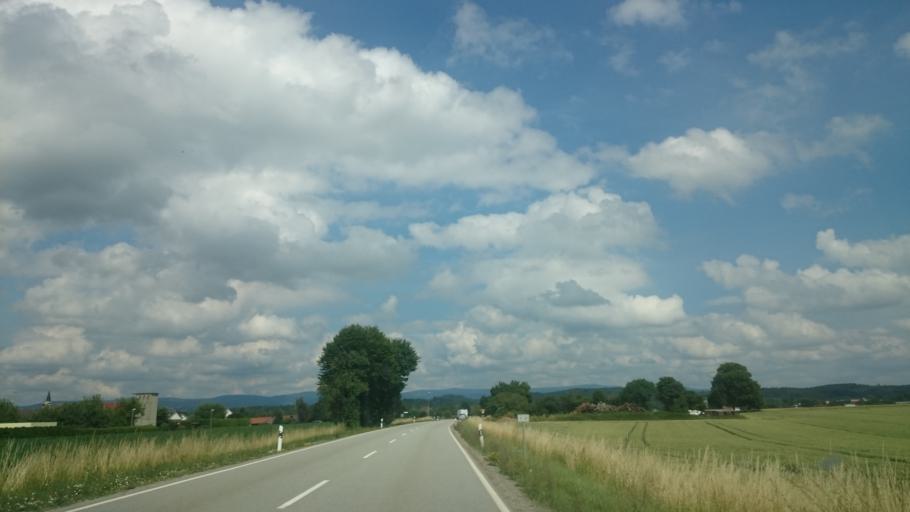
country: DE
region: Bavaria
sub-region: Lower Bavaria
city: Steinach
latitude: 48.9497
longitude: 12.6024
